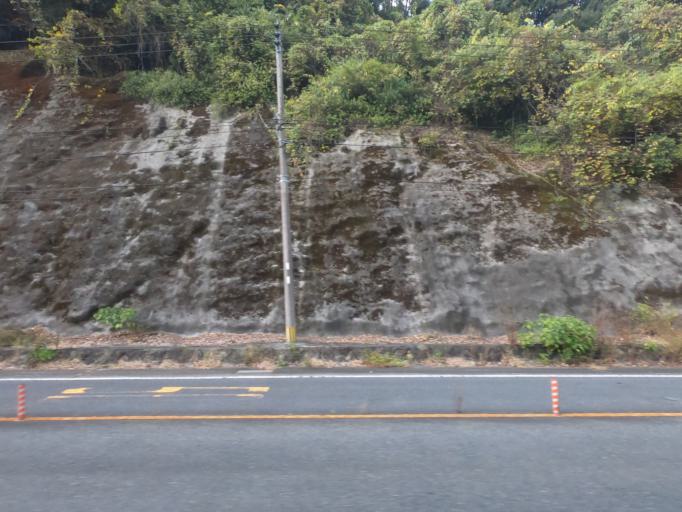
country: JP
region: Kumamoto
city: Minamata
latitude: 32.2469
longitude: 130.4956
